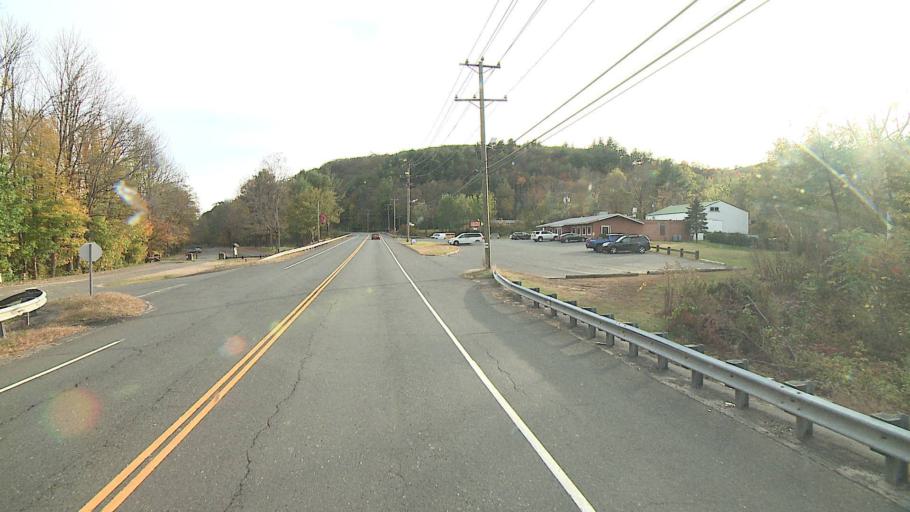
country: US
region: Connecticut
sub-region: Litchfield County
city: New Hartford Center
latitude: 41.8597
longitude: -72.9592
